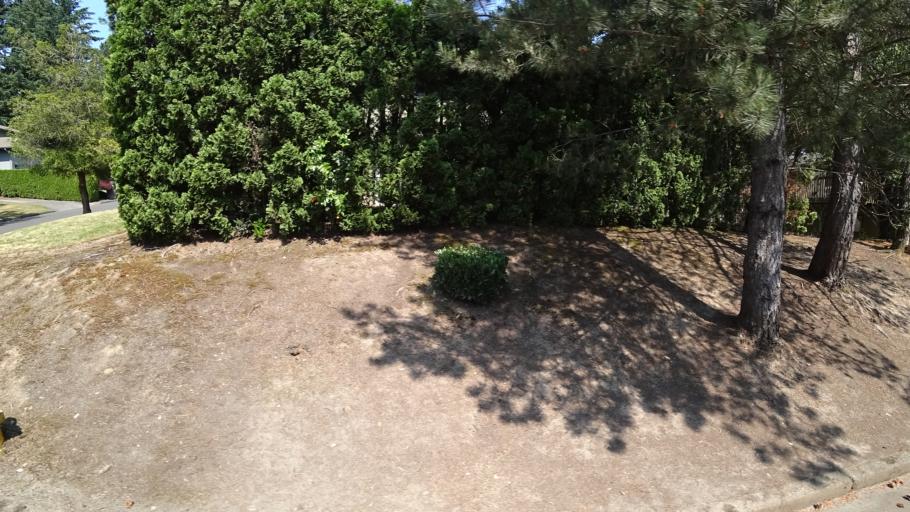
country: US
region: Oregon
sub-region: Clackamas County
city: Happy Valley
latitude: 45.4474
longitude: -122.5601
